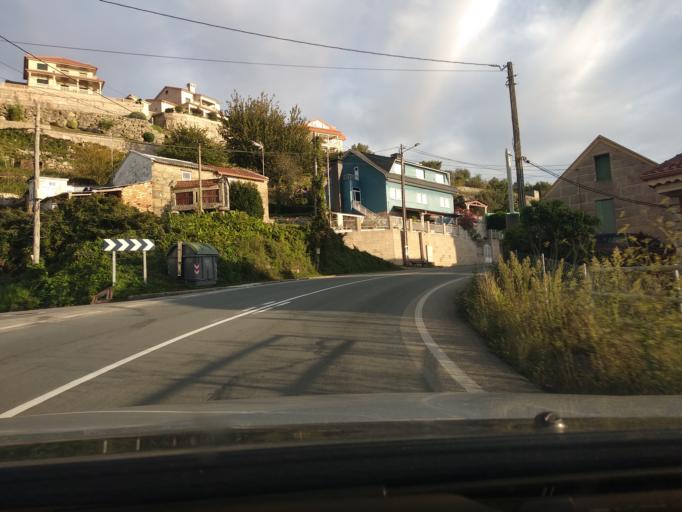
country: ES
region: Galicia
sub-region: Provincia de Pontevedra
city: Moana
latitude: 42.2842
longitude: -8.7137
